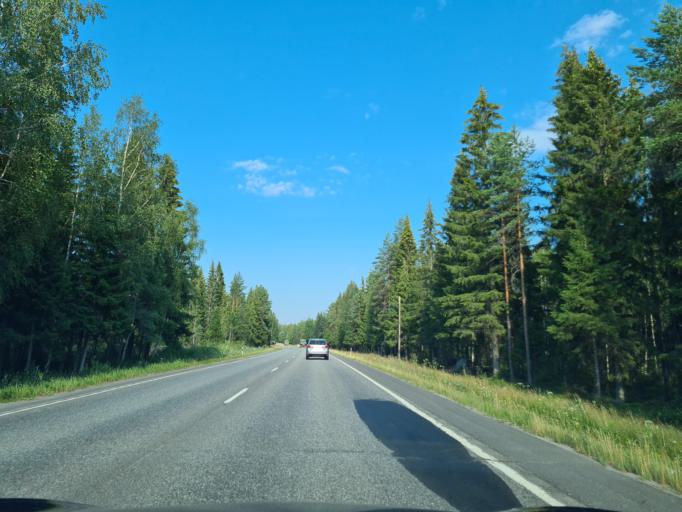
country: FI
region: Satakunta
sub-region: Pohjois-Satakunta
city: Kankaanpaeae
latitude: 61.8368
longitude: 22.4329
